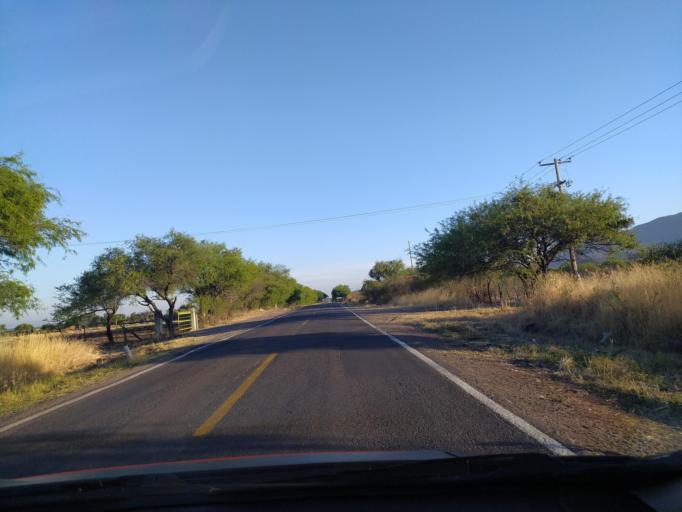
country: MX
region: Guanajuato
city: Ciudad Manuel Doblado
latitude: 20.7611
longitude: -101.8279
